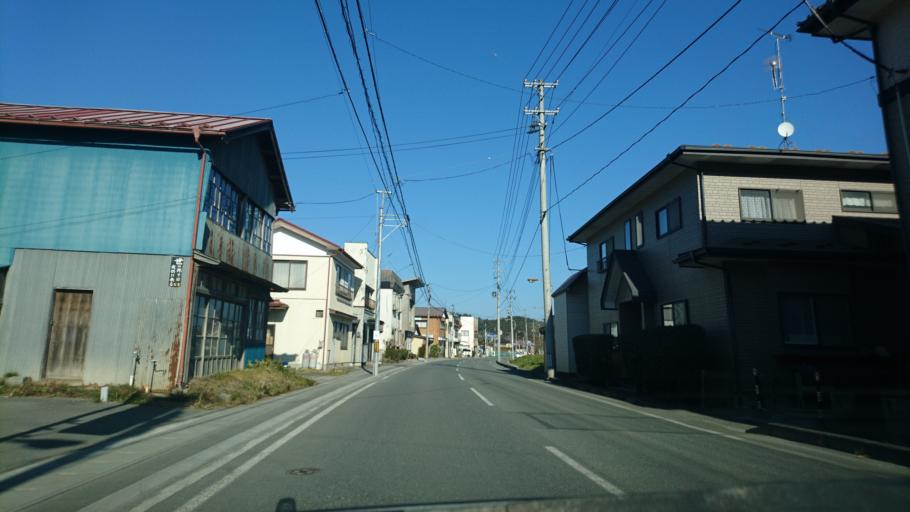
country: JP
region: Iwate
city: Ichinoseki
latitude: 38.9136
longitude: 141.3275
